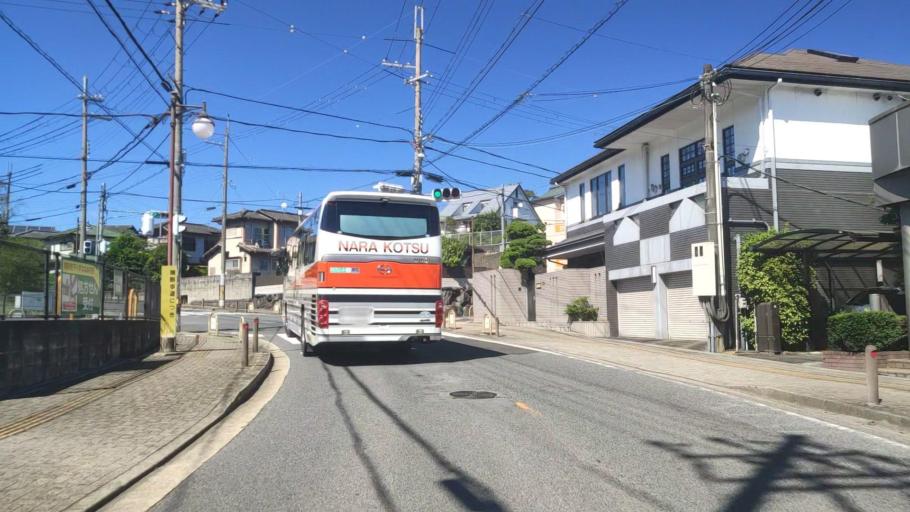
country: JP
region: Nara
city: Haibara-akanedai
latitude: 34.5342
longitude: 135.9491
